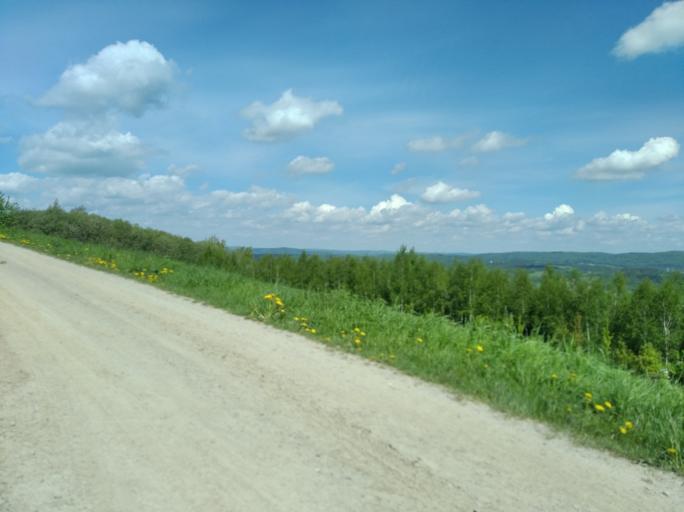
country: PL
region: Subcarpathian Voivodeship
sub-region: Powiat strzyzowski
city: Frysztak
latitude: 49.8346
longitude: 21.5299
